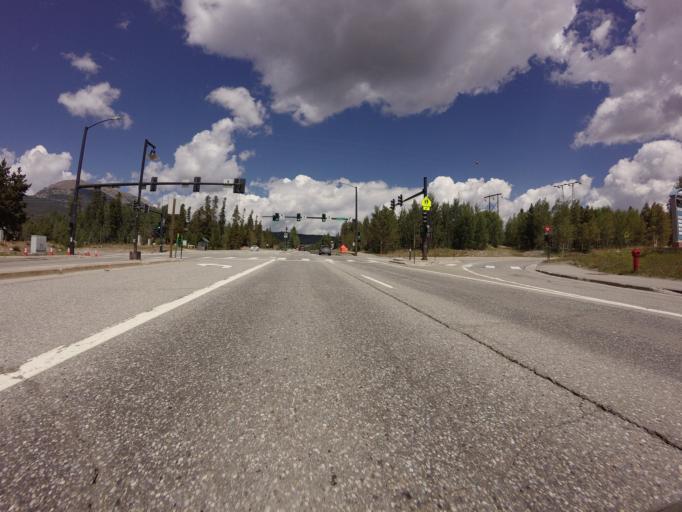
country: US
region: Colorado
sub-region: Summit County
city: Frisco
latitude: 39.5815
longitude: -106.0935
